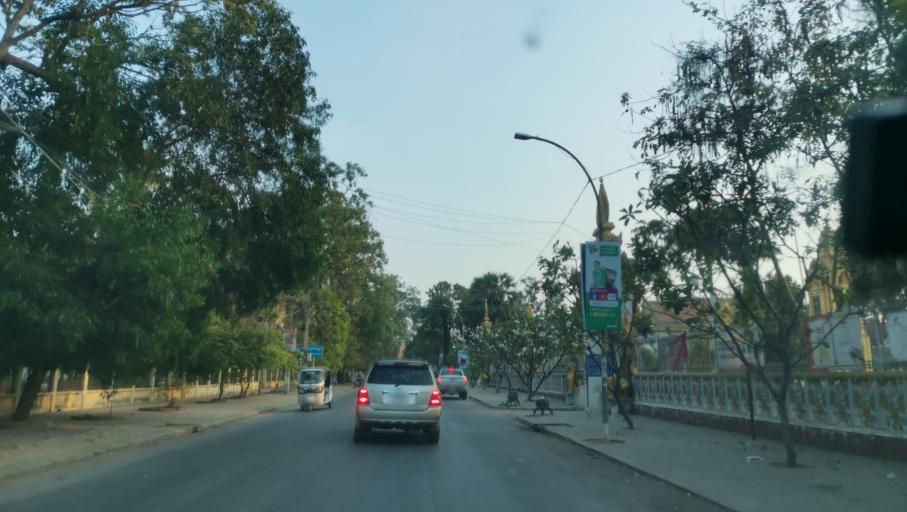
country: KH
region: Battambang
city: Battambang
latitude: 13.0880
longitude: 103.1980
